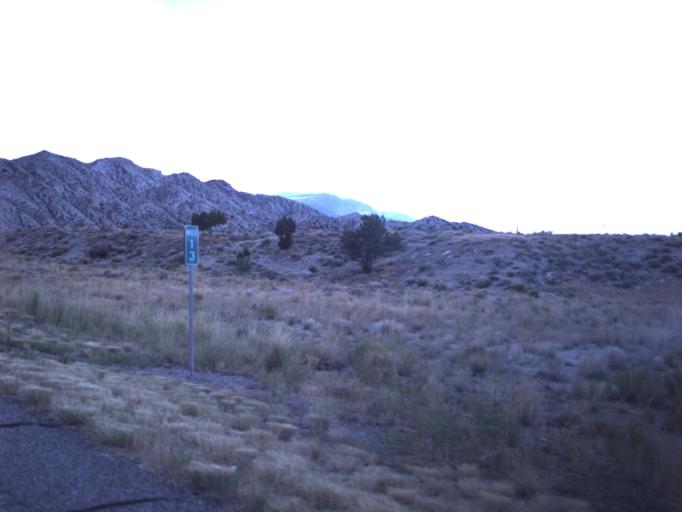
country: US
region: Utah
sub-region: Sevier County
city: Aurora
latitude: 38.8123
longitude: -111.9391
